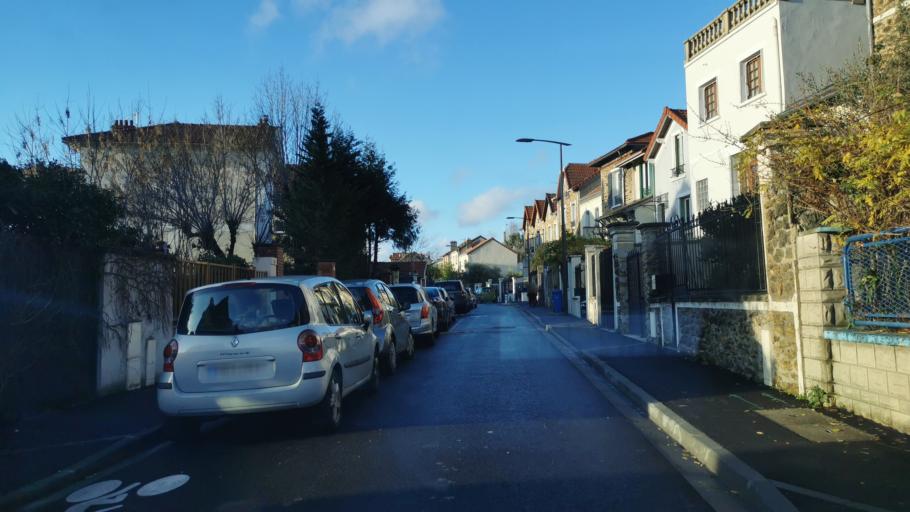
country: FR
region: Ile-de-France
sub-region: Departement de Seine-Saint-Denis
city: Rosny-sous-Bois
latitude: 48.8679
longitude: 2.4904
